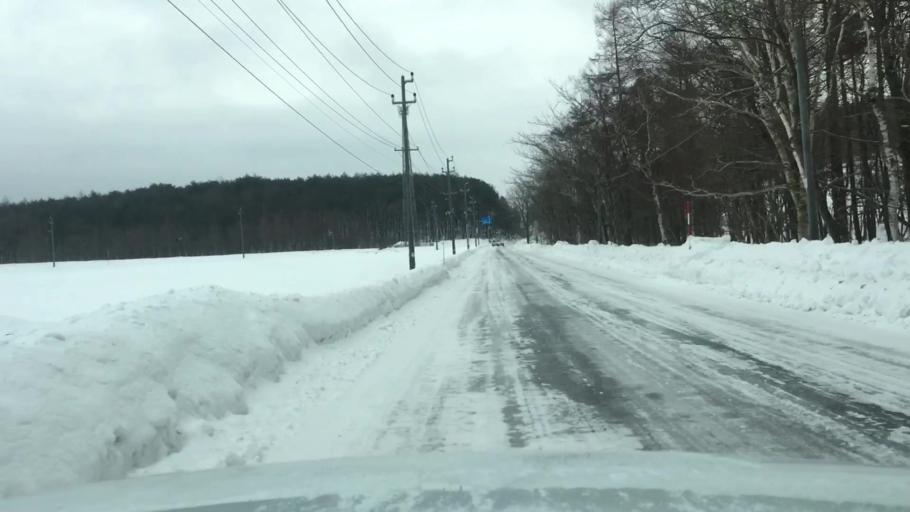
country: JP
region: Iwate
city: Shizukuishi
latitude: 39.9715
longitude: 140.9996
